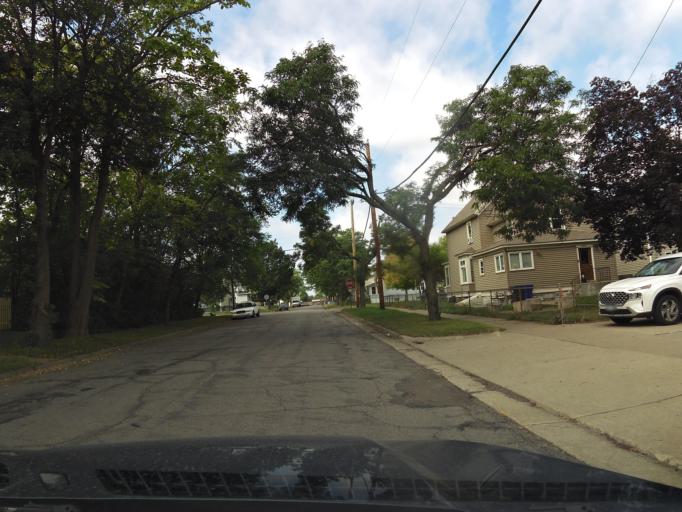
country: US
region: Minnesota
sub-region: Ramsey County
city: Saint Paul
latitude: 44.9600
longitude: -93.1030
